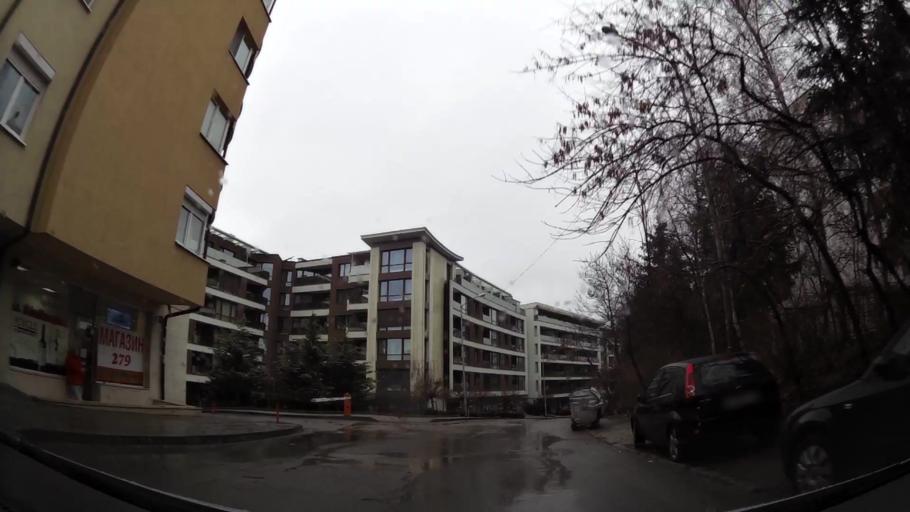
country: BG
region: Sofia-Capital
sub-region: Stolichna Obshtina
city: Sofia
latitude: 42.6379
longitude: 23.3668
